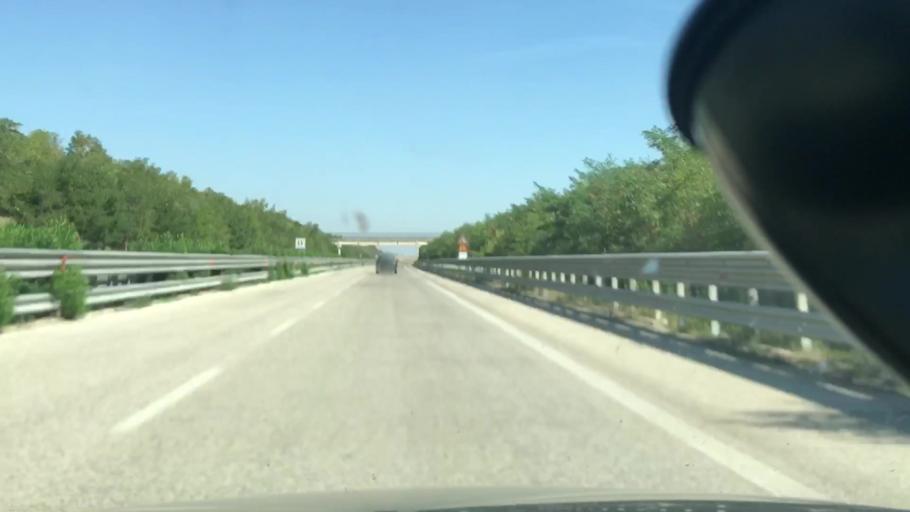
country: IT
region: Apulia
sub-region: Provincia di Foggia
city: Ordona
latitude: 41.2897
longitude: 15.5540
